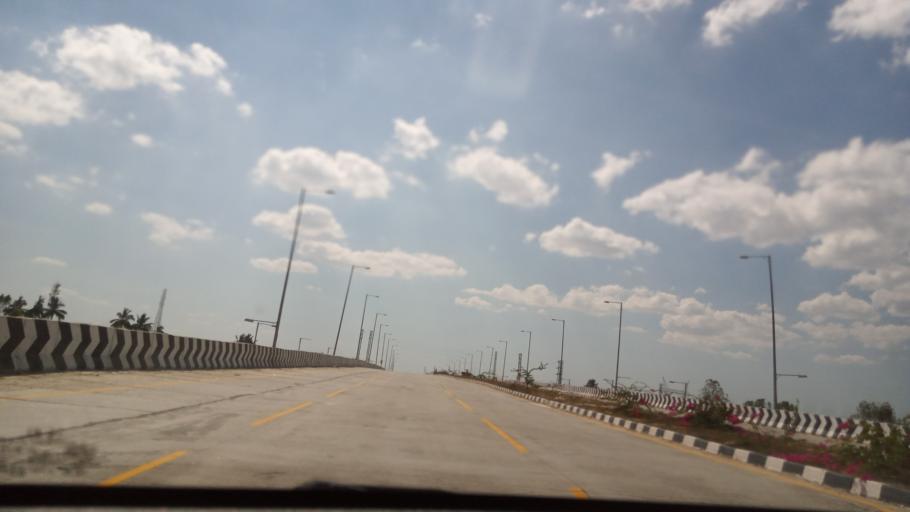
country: IN
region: Andhra Pradesh
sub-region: Chittoor
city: Palmaner
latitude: 13.2213
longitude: 78.7369
